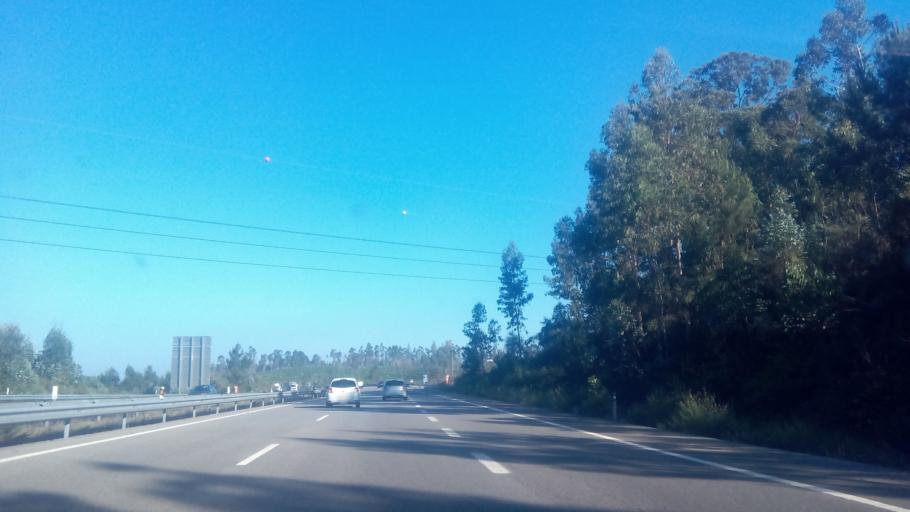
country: PT
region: Porto
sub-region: Pacos de Ferreira
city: Pacos de Ferreira
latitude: 41.2629
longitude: -8.3754
